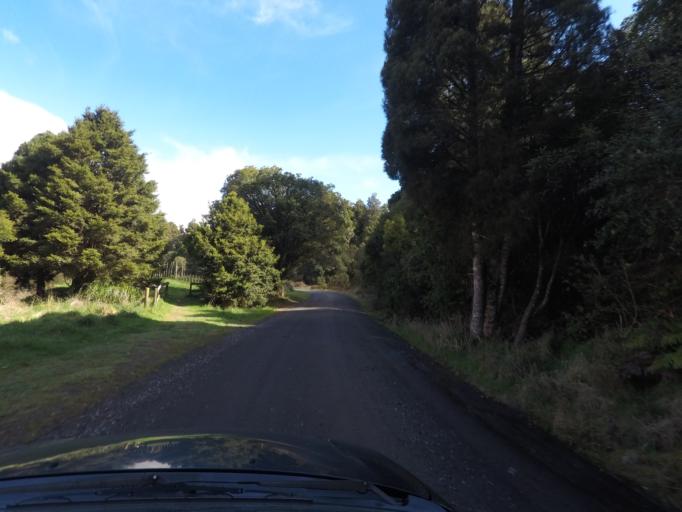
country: NZ
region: Manawatu-Wanganui
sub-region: Ruapehu District
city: Waiouru
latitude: -39.3948
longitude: 175.3964
